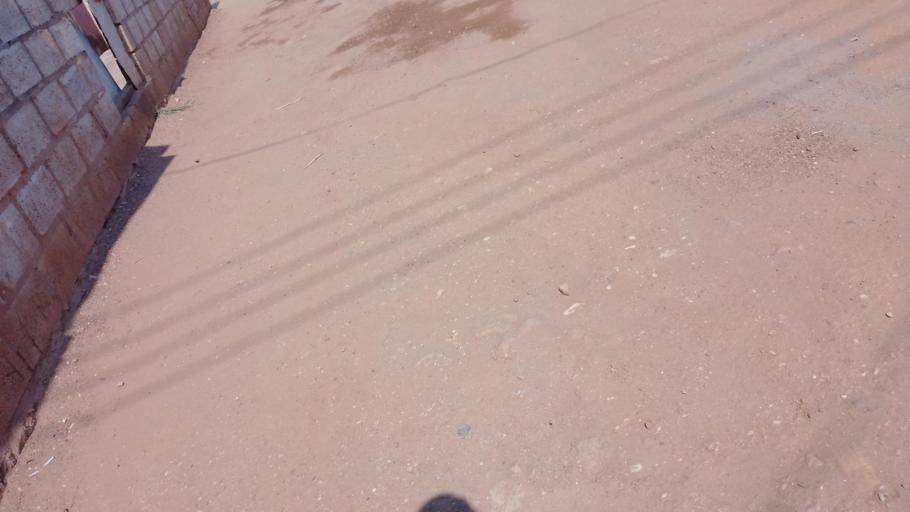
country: ZM
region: Lusaka
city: Lusaka
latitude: -15.3968
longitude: 28.3716
